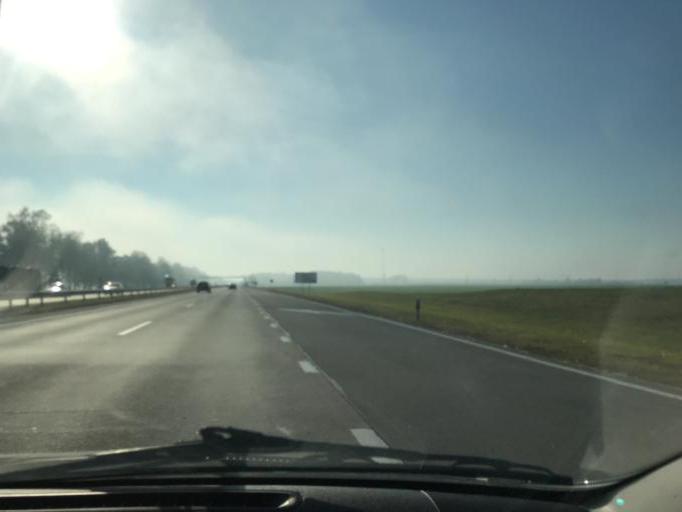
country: BY
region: Minsk
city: Samakhvalavichy
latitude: 53.5715
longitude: 27.4704
